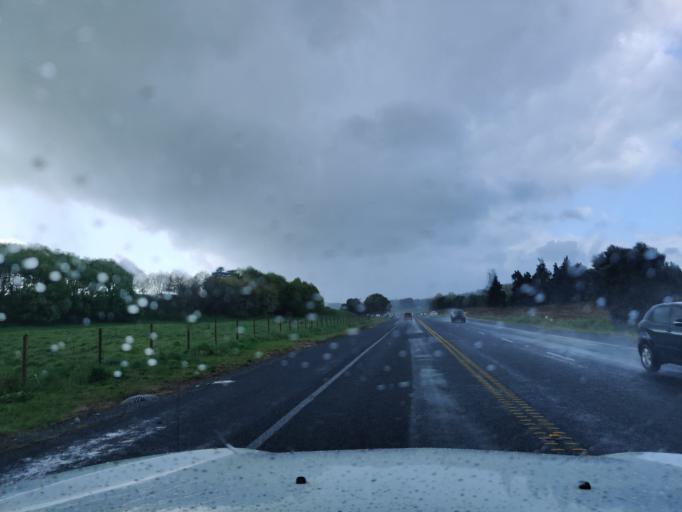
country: NZ
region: Waikato
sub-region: Waipa District
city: Cambridge
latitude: -37.9425
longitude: 175.5831
